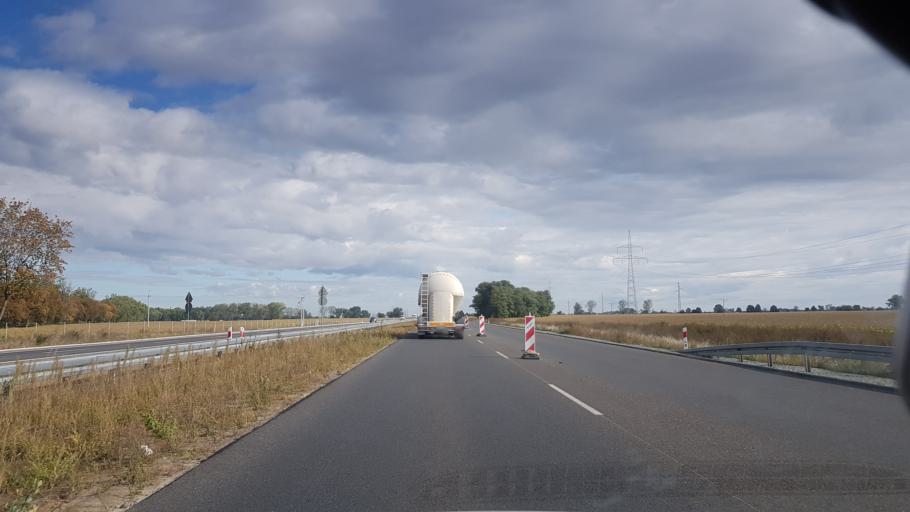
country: PL
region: Greater Poland Voivodeship
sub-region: Powiat poznanski
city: Steszew
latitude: 52.3186
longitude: 16.7132
